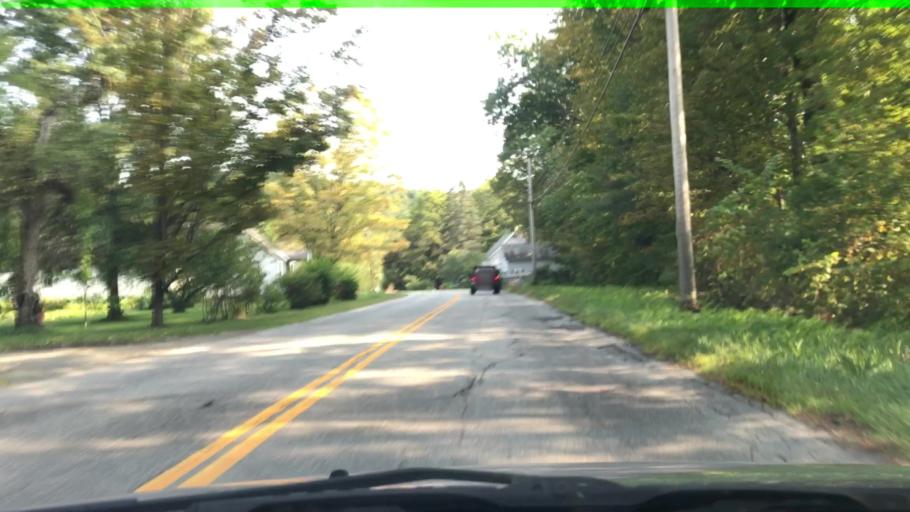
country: US
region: Vermont
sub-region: Windham County
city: Bellows Falls
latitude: 43.1136
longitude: -72.4246
